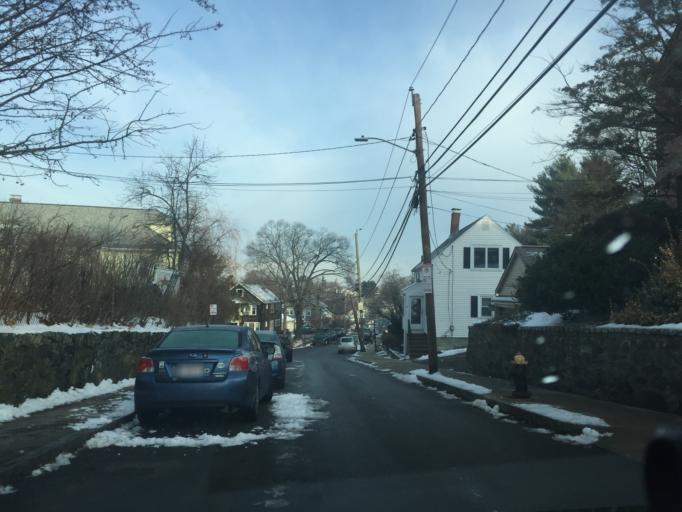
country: US
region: Massachusetts
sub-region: Middlesex County
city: Watertown
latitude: 42.3504
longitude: -71.1579
